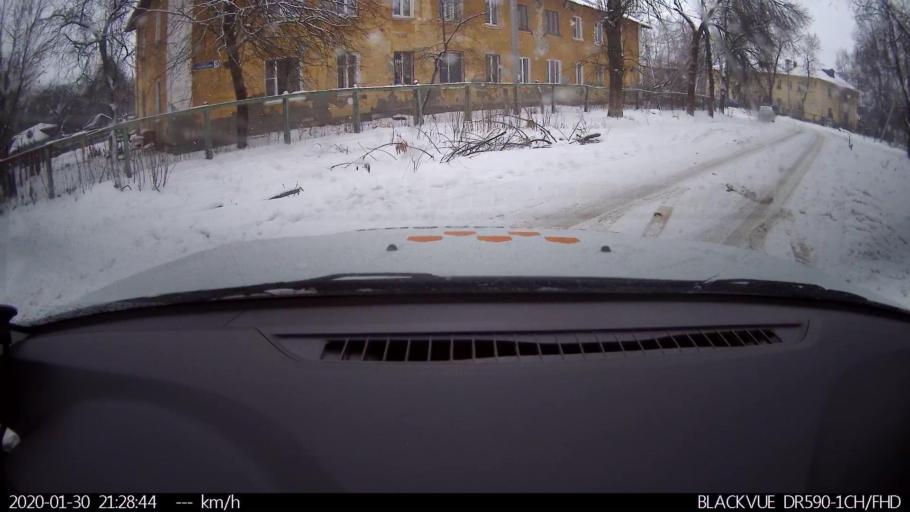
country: RU
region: Nizjnij Novgorod
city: Burevestnik
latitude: 56.2261
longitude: 43.8479
